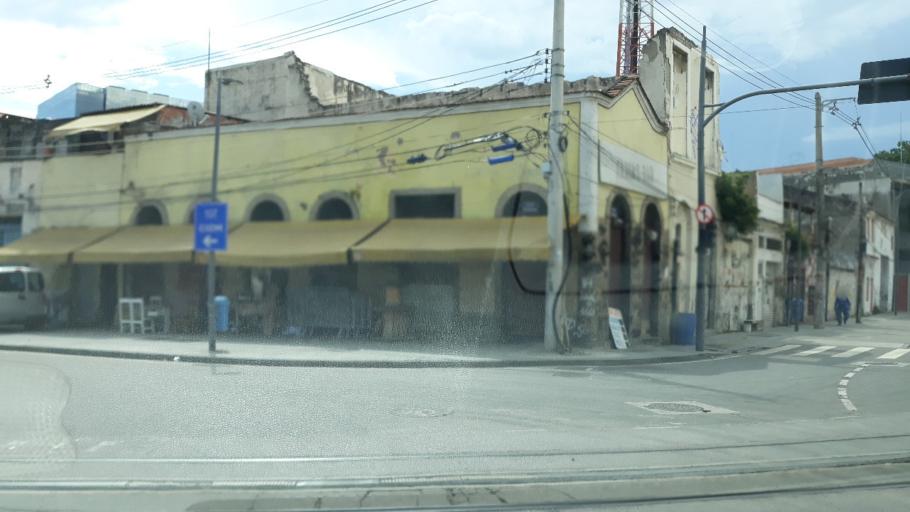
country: BR
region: Rio de Janeiro
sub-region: Rio De Janeiro
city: Rio de Janeiro
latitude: -22.8975
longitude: -43.1990
